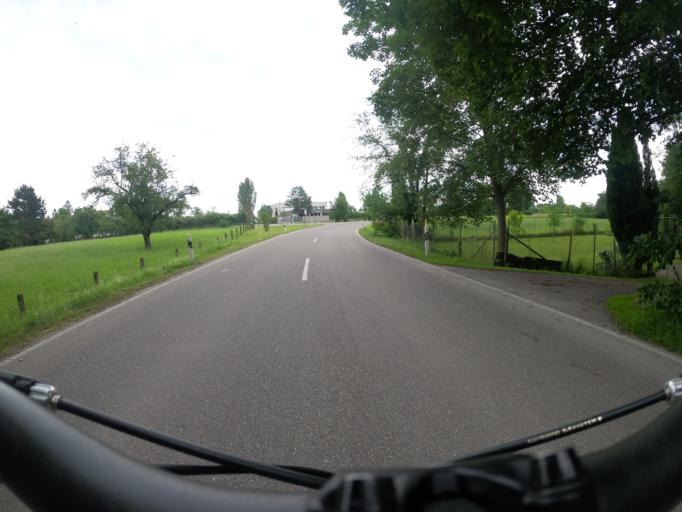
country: DE
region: Bavaria
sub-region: Swabia
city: Neu-Ulm
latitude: 48.4179
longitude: 10.0249
